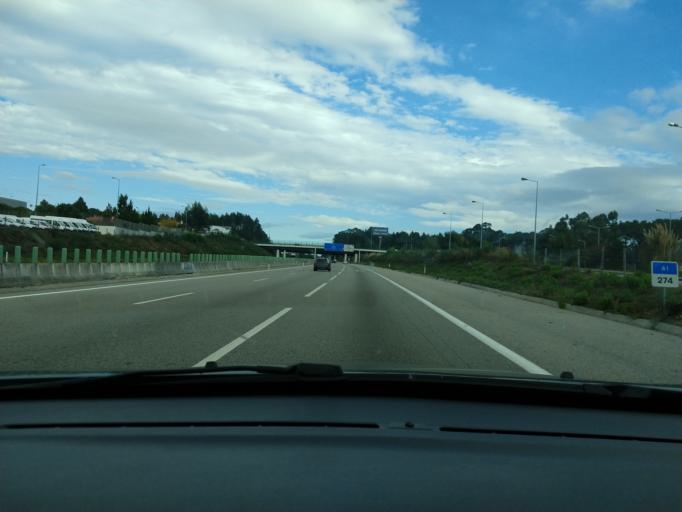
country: PT
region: Aveiro
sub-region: Santa Maria da Feira
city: Feira
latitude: 40.9212
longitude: -8.5675
